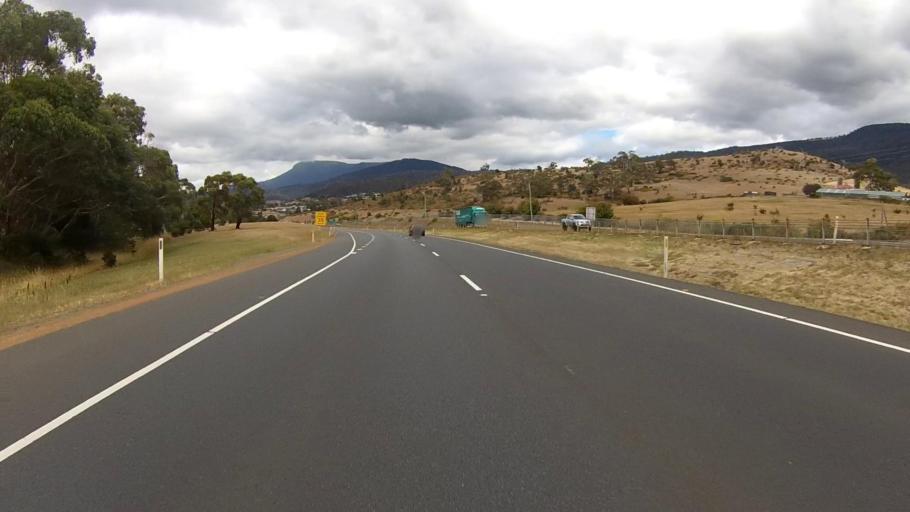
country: AU
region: Tasmania
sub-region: Glenorchy
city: Claremont
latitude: -42.7770
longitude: 147.2386
